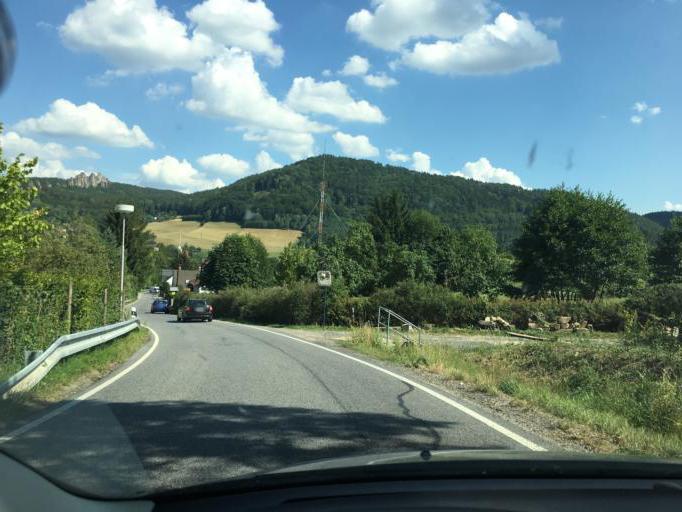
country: CZ
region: Liberecky
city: Mala Skala
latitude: 50.6397
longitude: 15.1844
